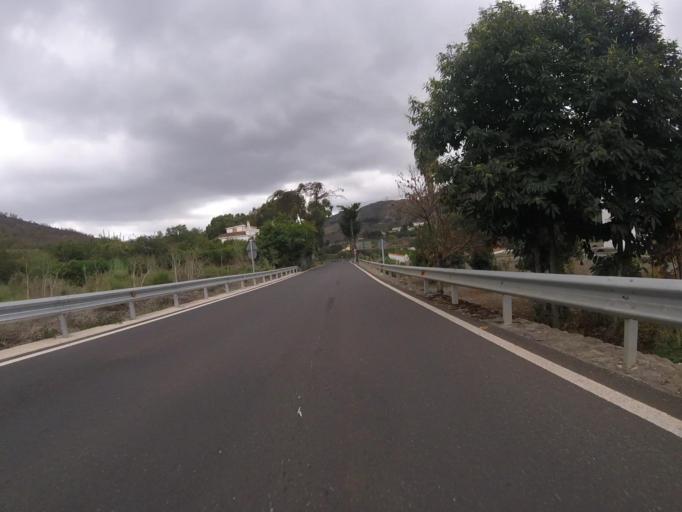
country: ES
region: Canary Islands
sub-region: Provincia de Las Palmas
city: Vega de San Mateo
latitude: 28.0092
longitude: -15.5432
